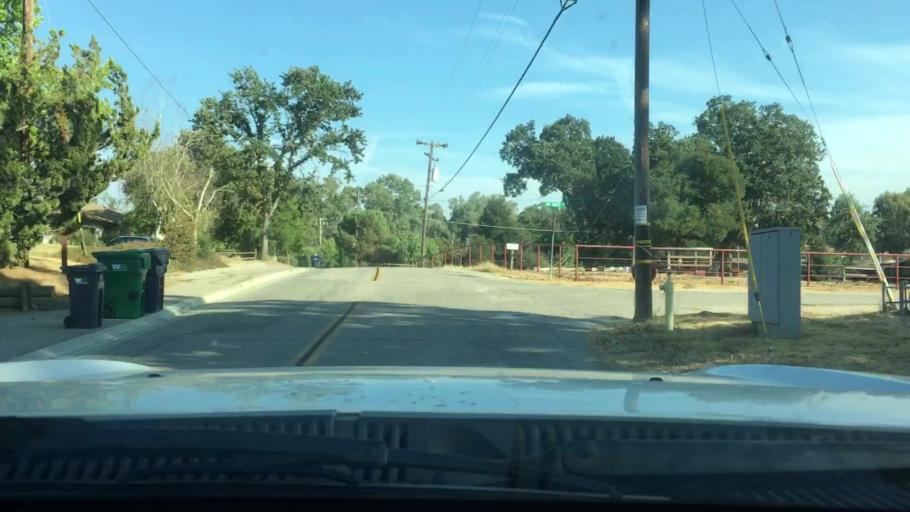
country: US
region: California
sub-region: San Luis Obispo County
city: Atascadero
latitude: 35.4619
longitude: -120.6742
